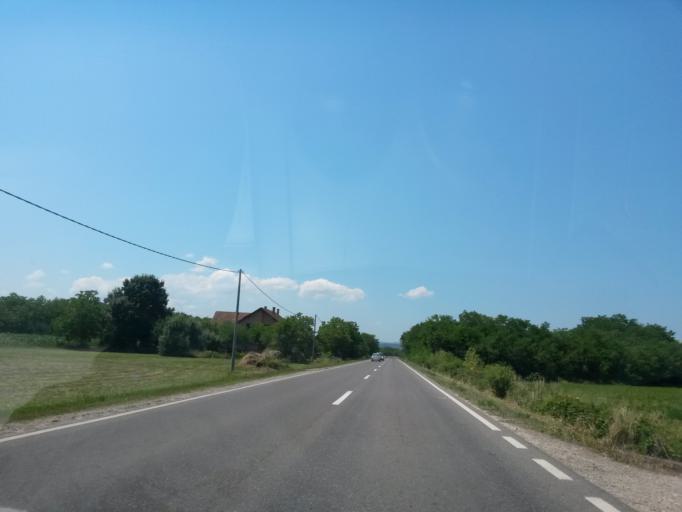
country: BA
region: Federation of Bosnia and Herzegovina
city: Odzak
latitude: 44.9737
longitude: 18.3536
